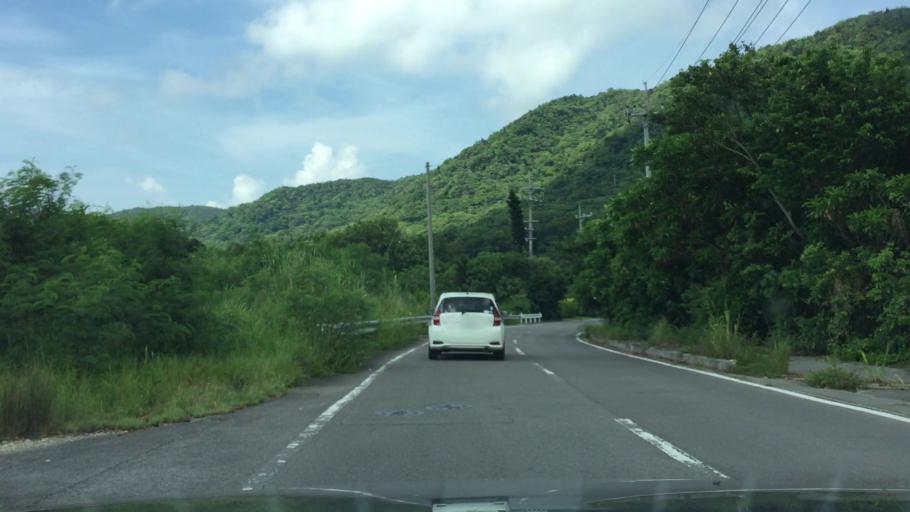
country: JP
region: Okinawa
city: Ishigaki
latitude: 24.4557
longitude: 124.2249
